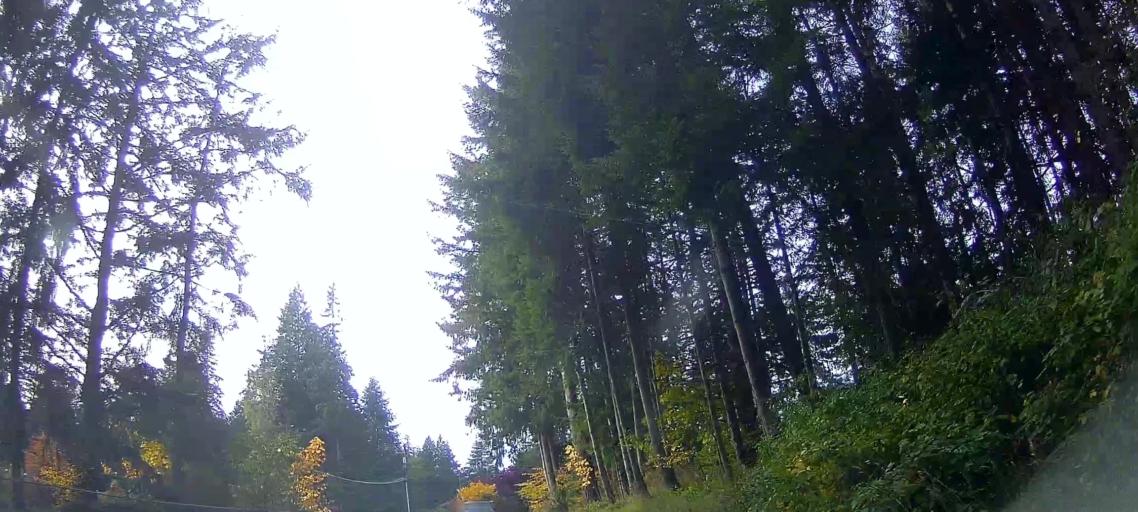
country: US
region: Washington
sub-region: Snohomish County
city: Stanwood
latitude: 48.2845
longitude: -122.3479
